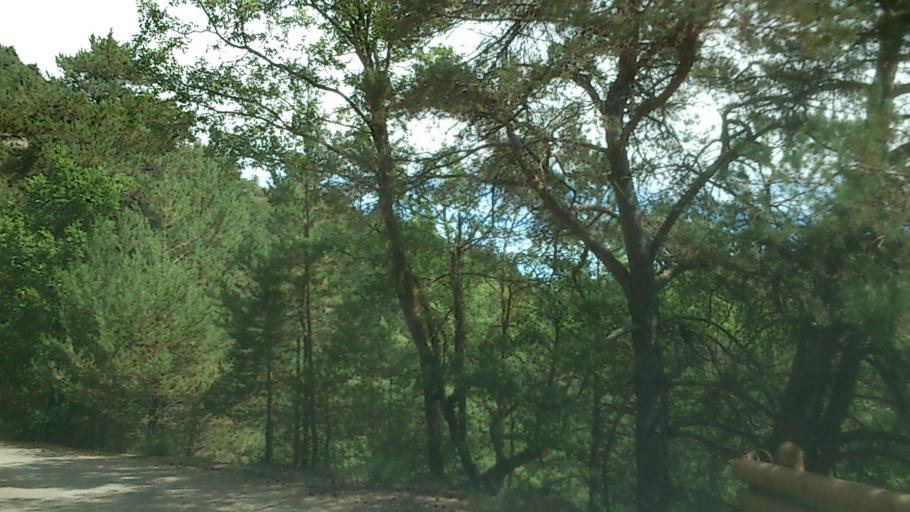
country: ES
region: Aragon
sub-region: Provincia de Huesca
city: Yebra de Basa
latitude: 42.3244
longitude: -0.2646
